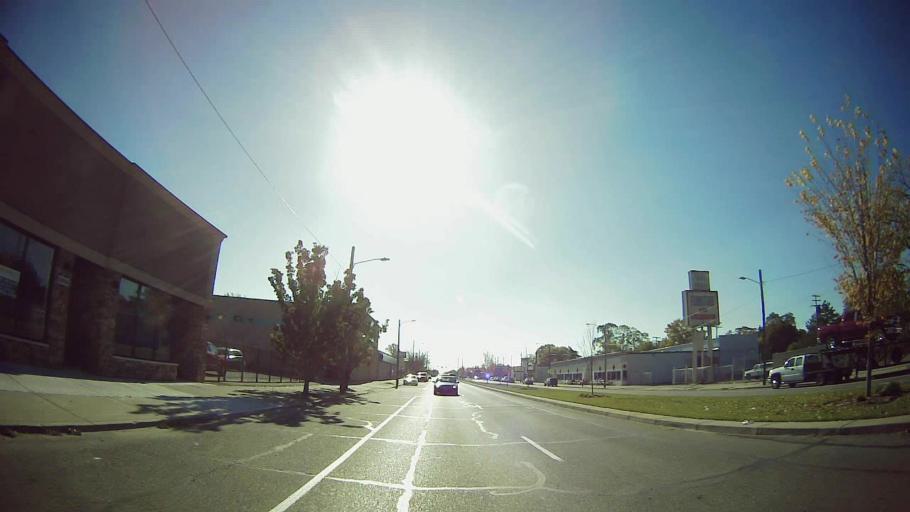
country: US
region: Michigan
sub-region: Oakland County
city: Ferndale
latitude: 42.4431
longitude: -83.1418
